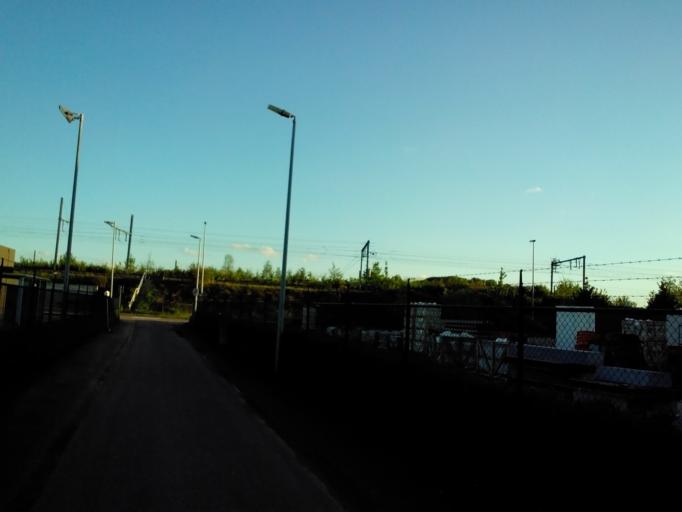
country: BE
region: Flanders
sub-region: Provincie Vlaams-Brabant
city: Leuven
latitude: 50.9025
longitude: 4.7052
